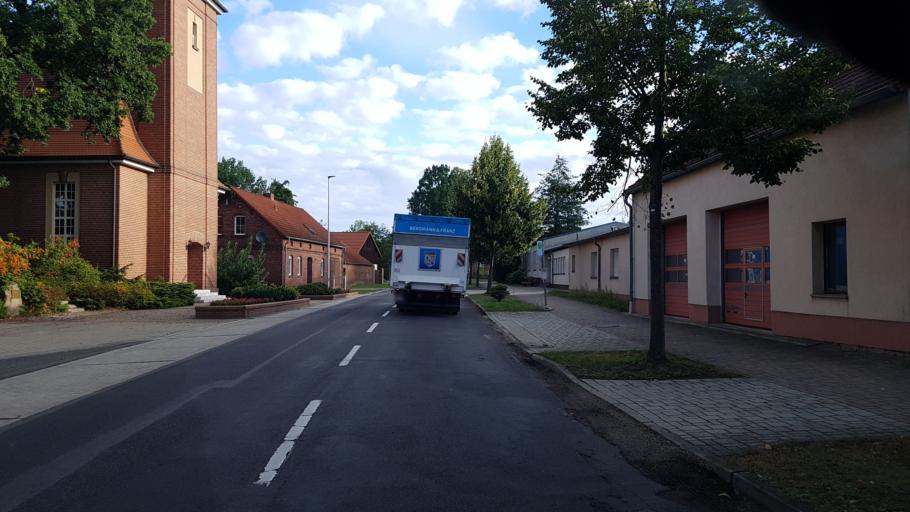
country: DE
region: Brandenburg
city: Welzow
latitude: 51.5520
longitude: 14.1896
